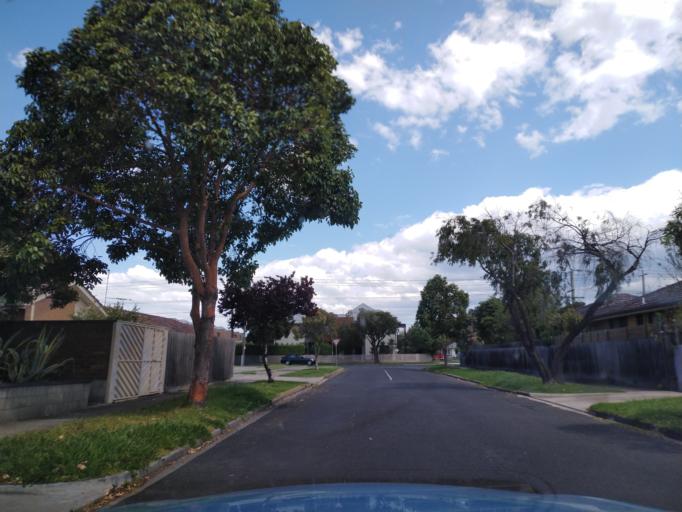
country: AU
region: Victoria
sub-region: Hobsons Bay
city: South Kingsville
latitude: -37.8333
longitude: 144.8733
